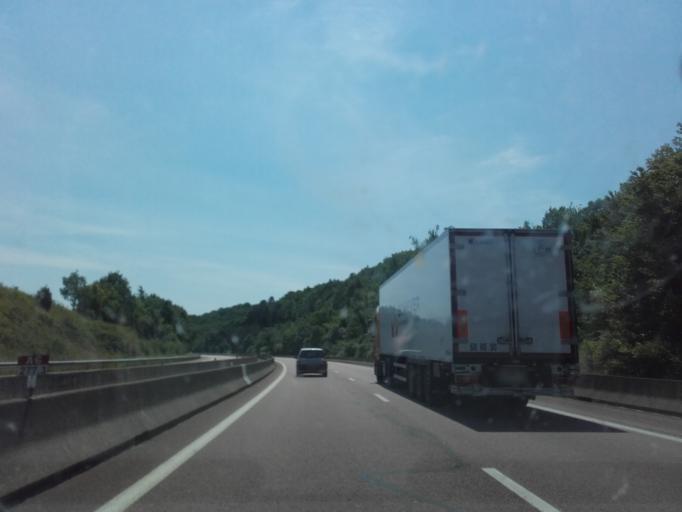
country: FR
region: Bourgogne
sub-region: Departement de la Cote-d'Or
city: Pouilly-en-Auxois
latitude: 47.1802
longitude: 4.6808
